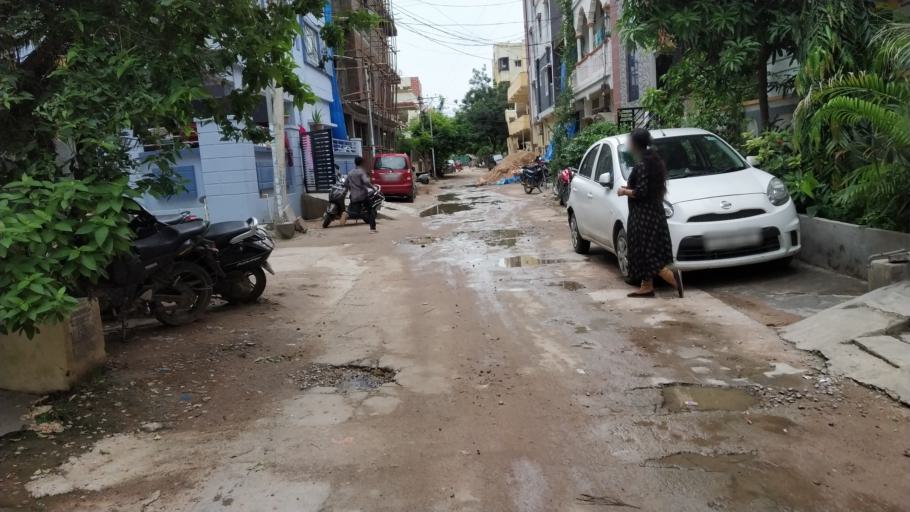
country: IN
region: Telangana
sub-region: Medak
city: Serilingampalle
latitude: 17.5092
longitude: 78.3055
